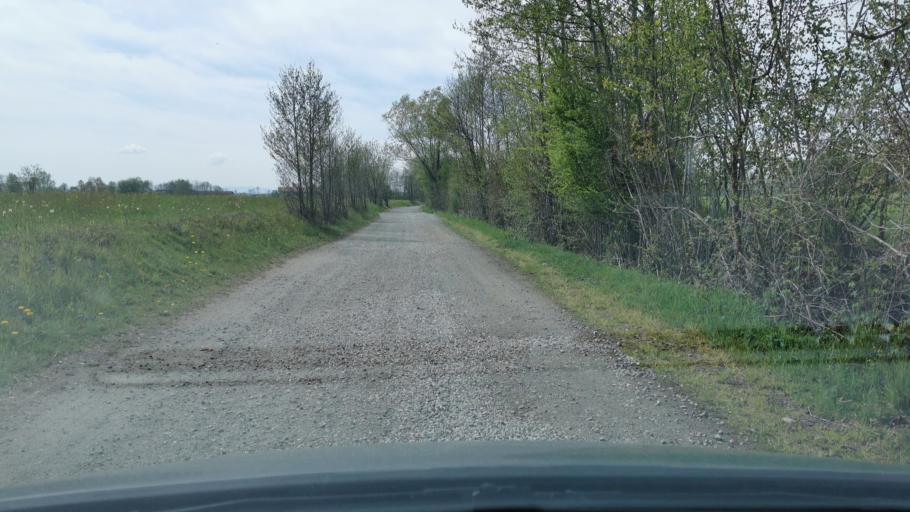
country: IT
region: Piedmont
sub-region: Provincia di Torino
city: San Ponso
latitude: 45.3403
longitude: 7.6714
